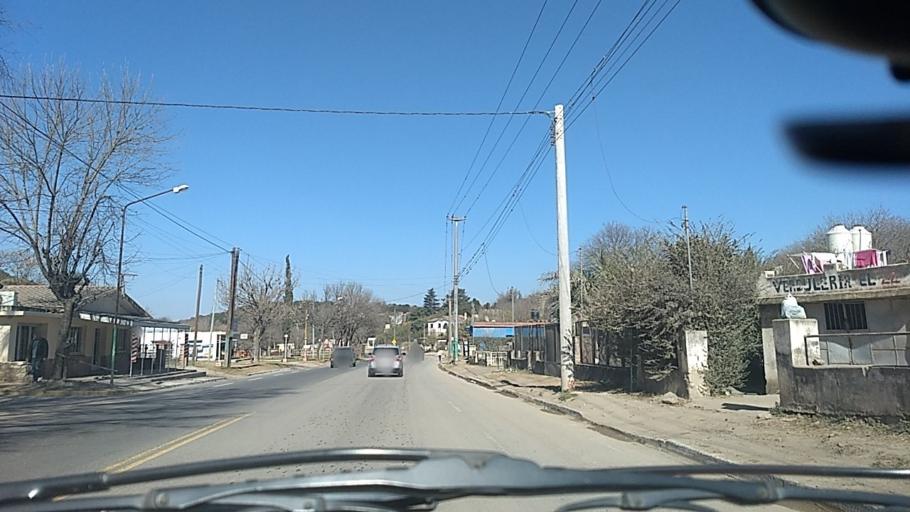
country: AR
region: Cordoba
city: Salsipuedes
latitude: -31.1051
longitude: -64.2921
